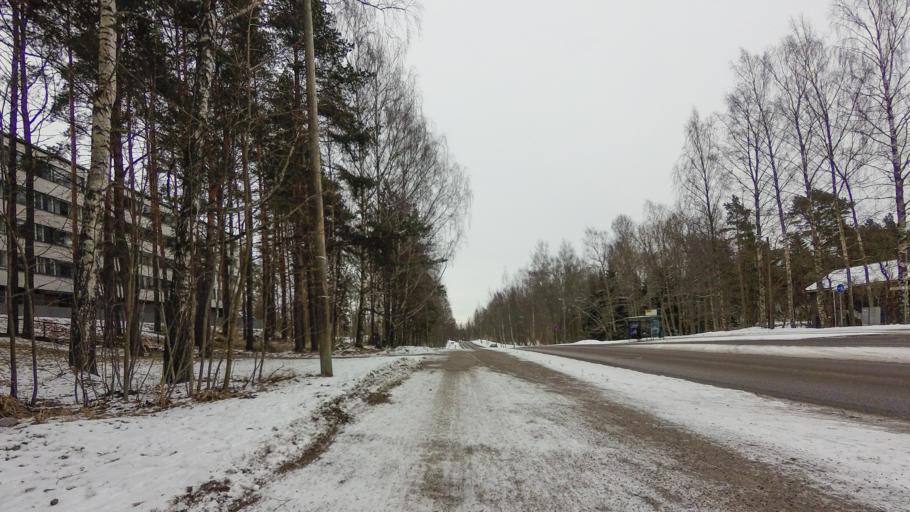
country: FI
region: Uusimaa
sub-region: Helsinki
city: Helsinki
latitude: 60.1749
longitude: 25.0411
